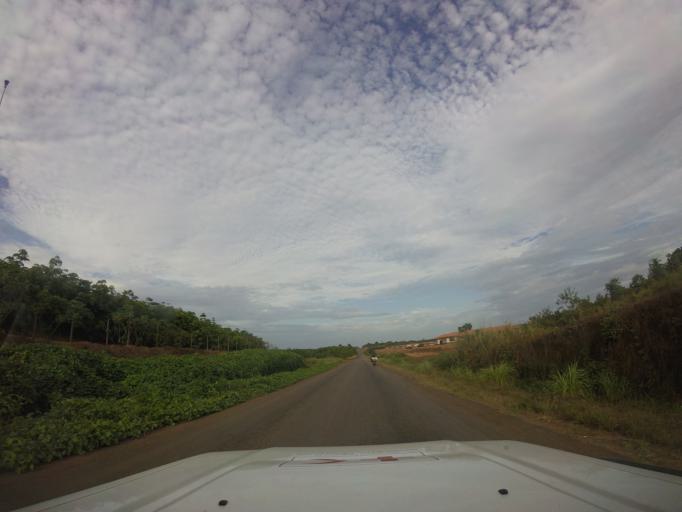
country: LR
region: Bomi
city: Tubmanburg
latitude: 6.7299
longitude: -11.0151
